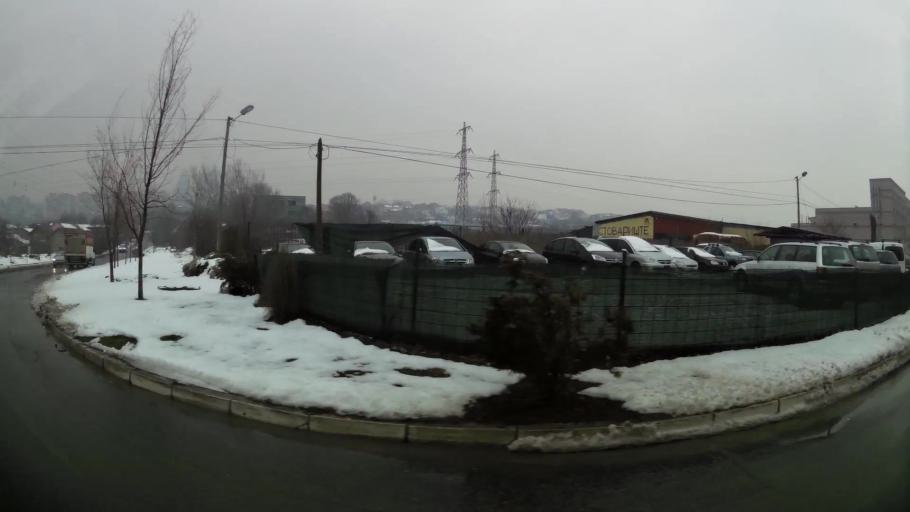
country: RS
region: Central Serbia
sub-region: Belgrade
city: Zvezdara
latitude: 44.7750
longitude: 20.5093
